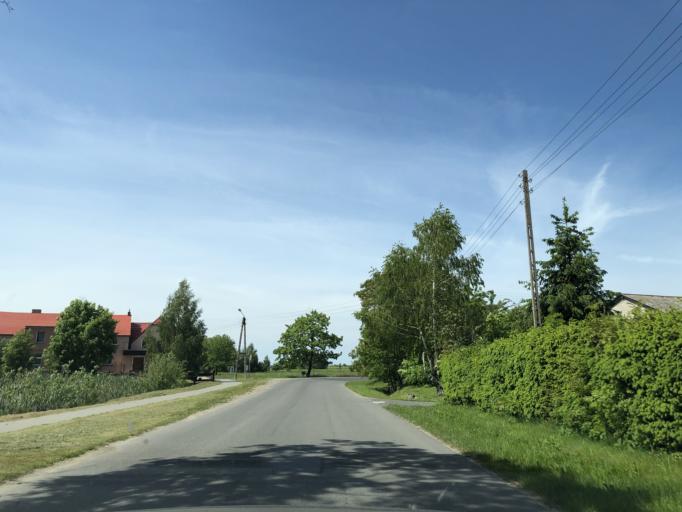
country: PL
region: West Pomeranian Voivodeship
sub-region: Powiat kolobrzeski
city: Dygowo
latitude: 54.1109
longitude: 15.7046
